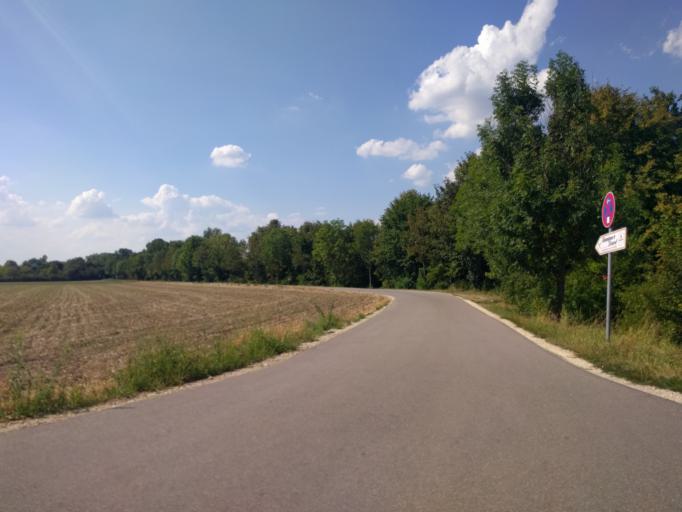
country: DE
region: Bavaria
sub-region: Upper Palatinate
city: Barbing
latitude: 49.0073
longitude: 12.2635
